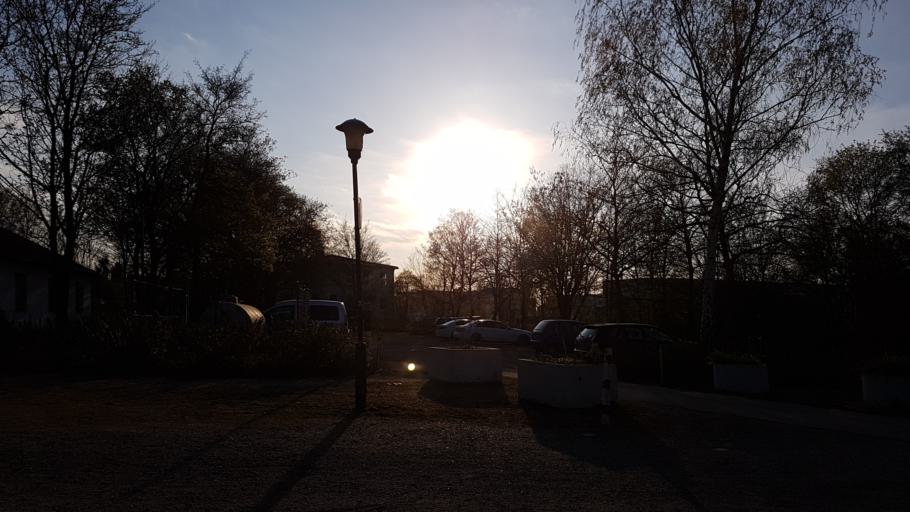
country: DE
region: Lower Saxony
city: Ronnenberg
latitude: 52.3466
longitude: 9.6812
